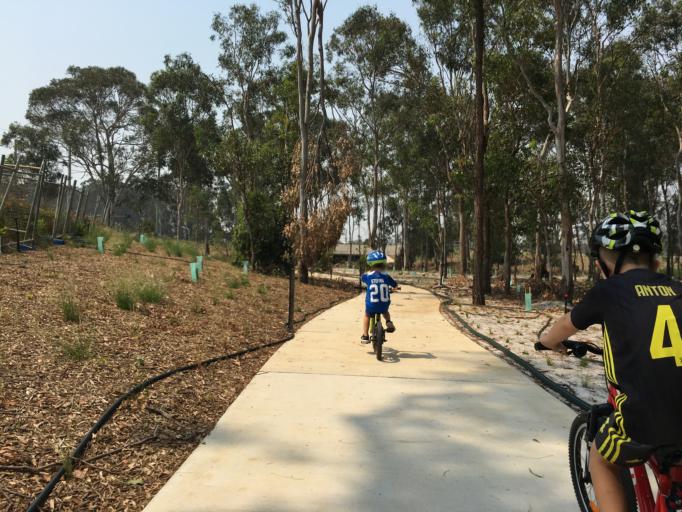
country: AU
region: New South Wales
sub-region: Campbelltown Municipality
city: Denham Court
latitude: -33.9731
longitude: 150.8169
